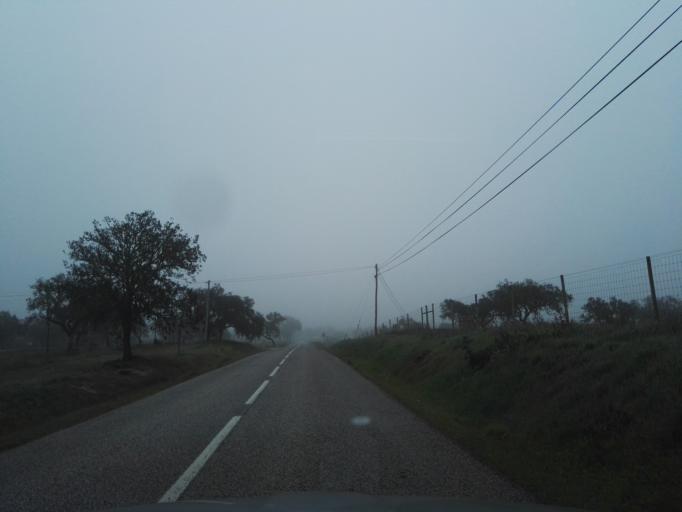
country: PT
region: Evora
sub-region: Montemor-O-Novo
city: Montemor-o-Novo
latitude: 38.7778
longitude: -8.2100
